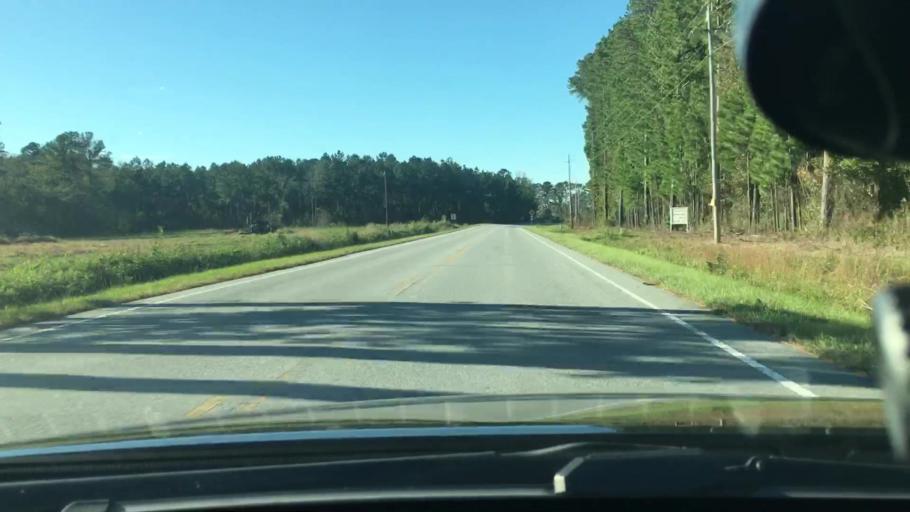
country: US
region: North Carolina
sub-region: Craven County
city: Vanceboro
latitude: 35.4152
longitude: -77.2531
